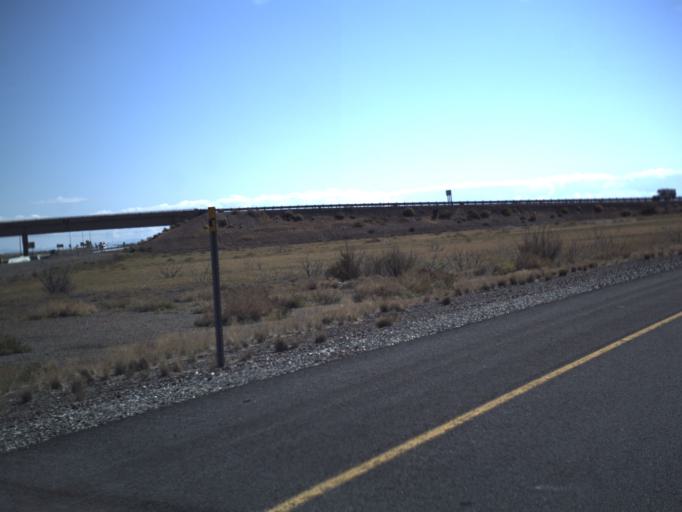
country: US
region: Utah
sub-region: Tooele County
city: Wendover
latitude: 40.7421
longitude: -113.9738
